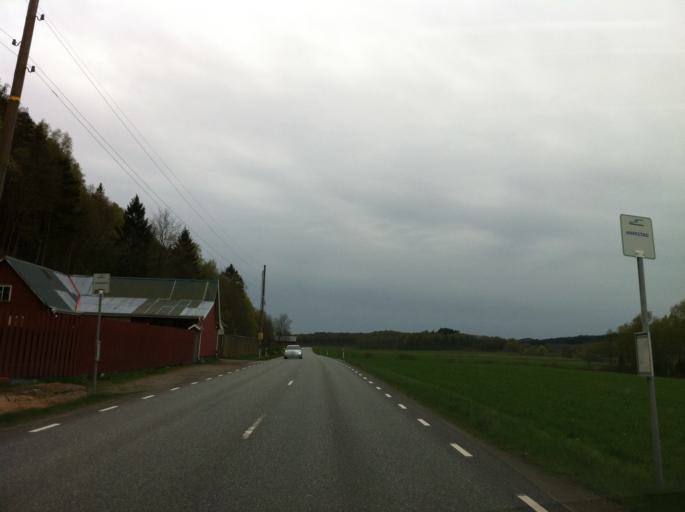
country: SE
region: Halland
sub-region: Falkenbergs Kommun
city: Falkenberg
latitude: 57.0497
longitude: 12.6104
